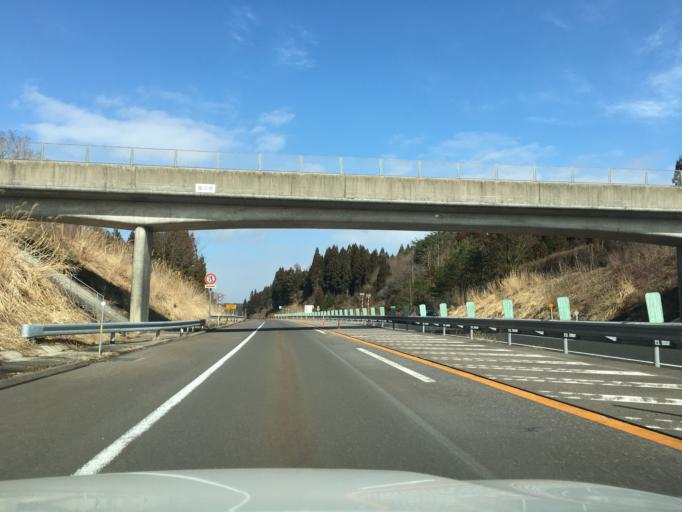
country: JP
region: Akita
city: Akita
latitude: 39.7287
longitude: 140.1798
